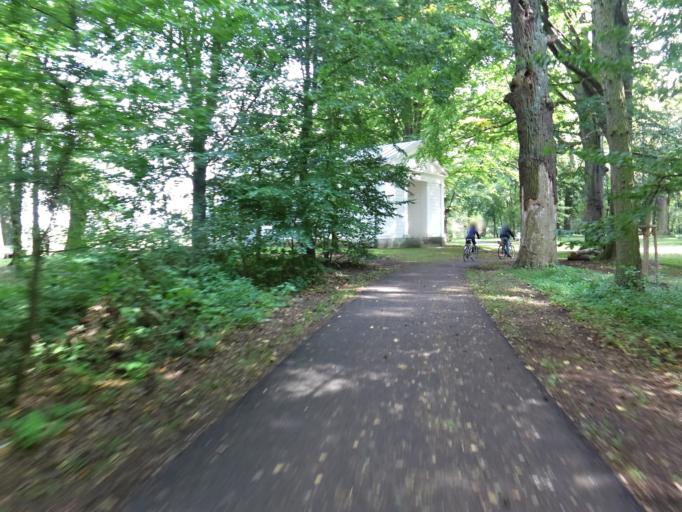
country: DE
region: Saxony-Anhalt
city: Vockerode
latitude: 51.8667
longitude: 12.3207
